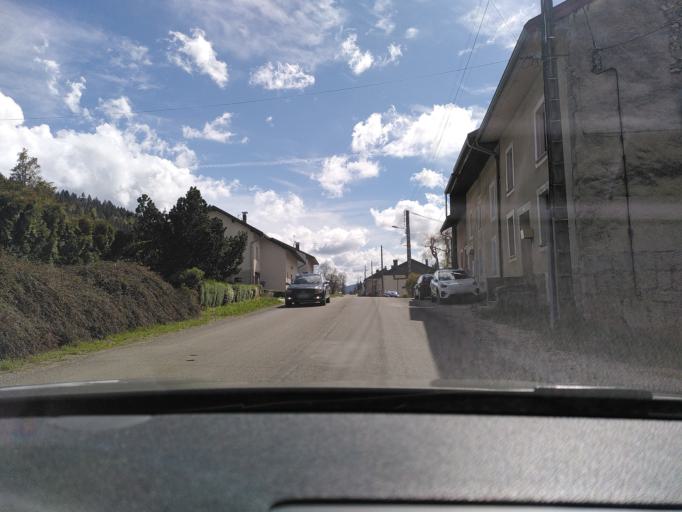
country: FR
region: Franche-Comte
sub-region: Departement du Jura
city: Les Rousses
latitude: 46.5263
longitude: 6.1297
